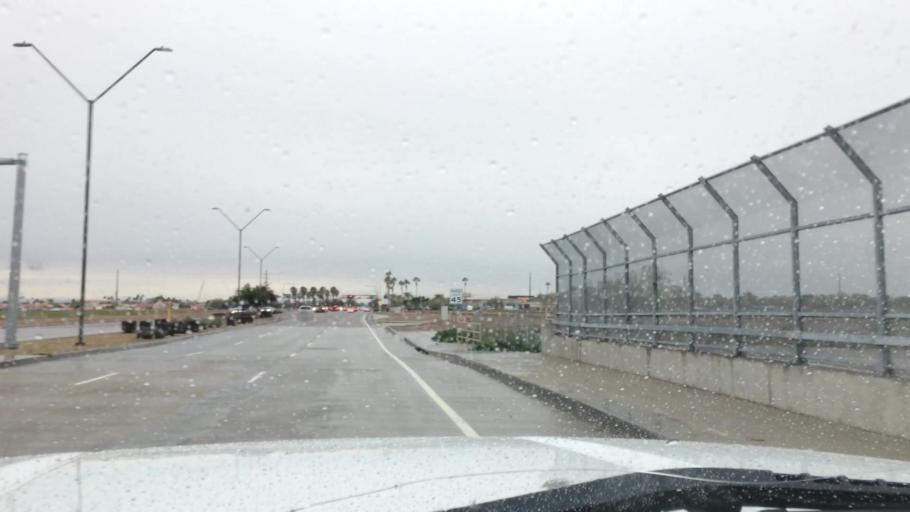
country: US
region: Arizona
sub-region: Maricopa County
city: Tolleson
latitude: 33.4606
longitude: -112.3067
